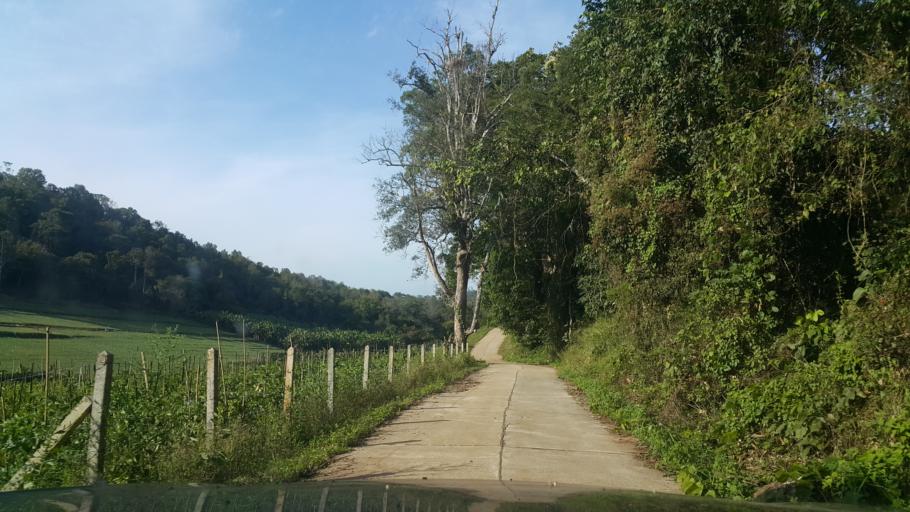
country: TH
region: Chiang Mai
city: Samoeng
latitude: 18.9914
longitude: 98.6844
